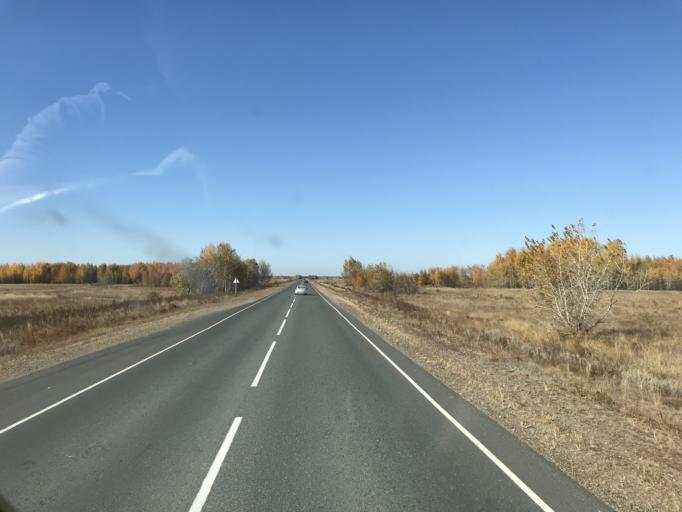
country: KZ
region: East Kazakhstan
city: Semey
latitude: 50.7081
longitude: 79.7316
